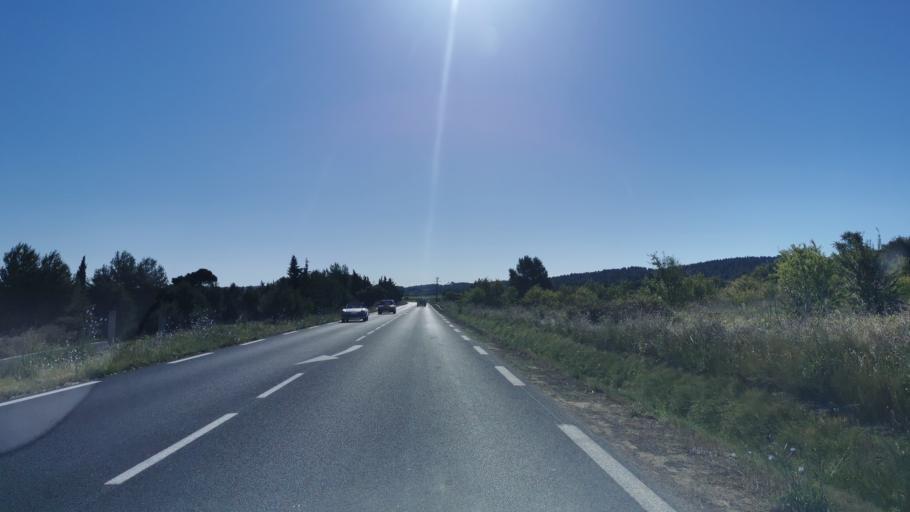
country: FR
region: Languedoc-Roussillon
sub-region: Departement de l'Herault
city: Nissan-lez-Enserune
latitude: 43.2767
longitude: 3.0884
